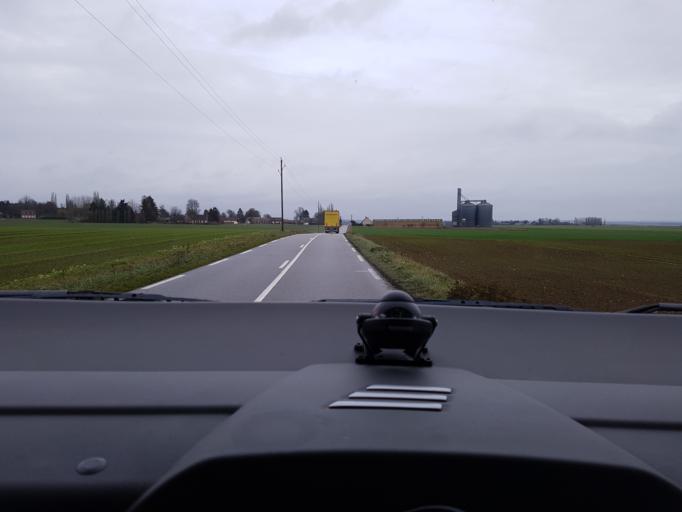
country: FR
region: Haute-Normandie
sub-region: Departement de l'Eure
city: Etrepagny
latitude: 49.3573
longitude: 1.5496
